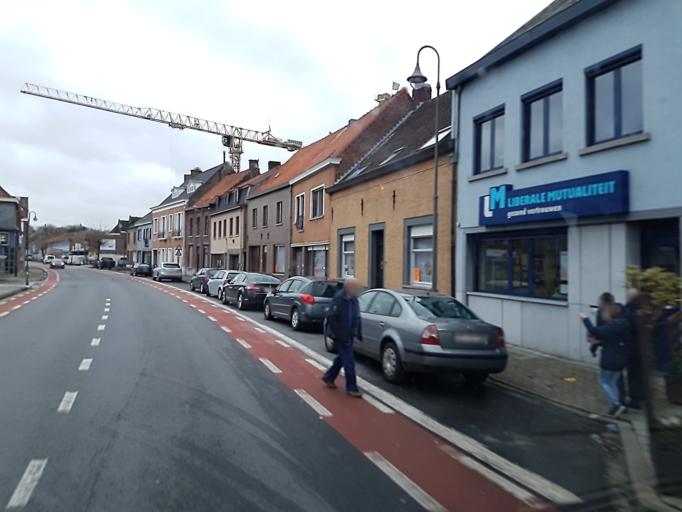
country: BE
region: Flanders
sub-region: Provincie Oost-Vlaanderen
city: Gavere
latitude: 50.9565
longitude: 3.6415
